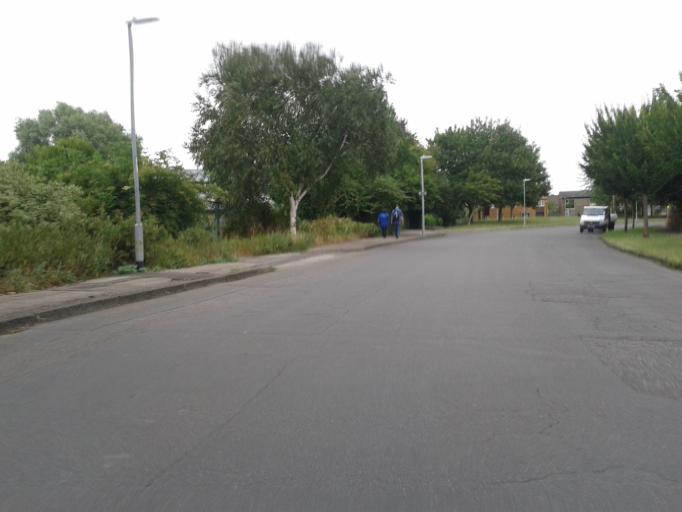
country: GB
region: England
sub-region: Cambridgeshire
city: Cambridge
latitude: 52.2171
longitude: 0.1597
